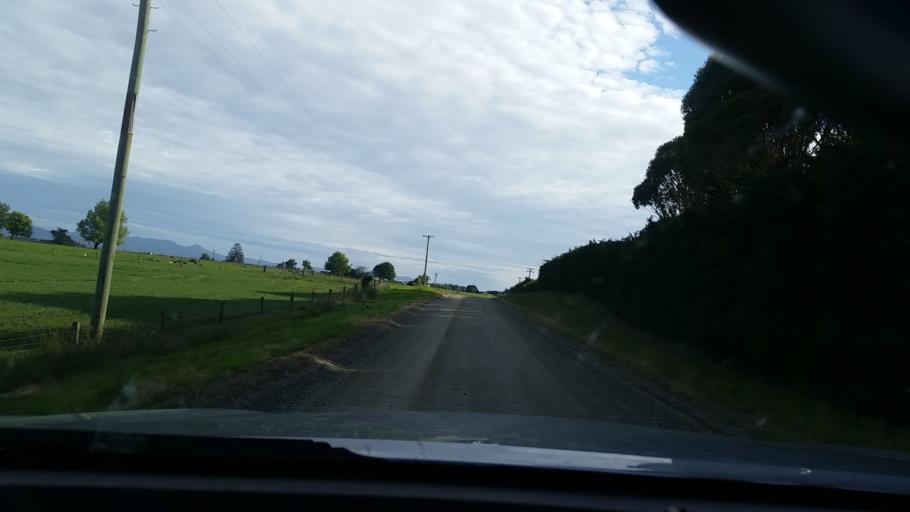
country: NZ
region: Southland
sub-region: Gore District
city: Gore
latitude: -46.2500
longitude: 168.7510
